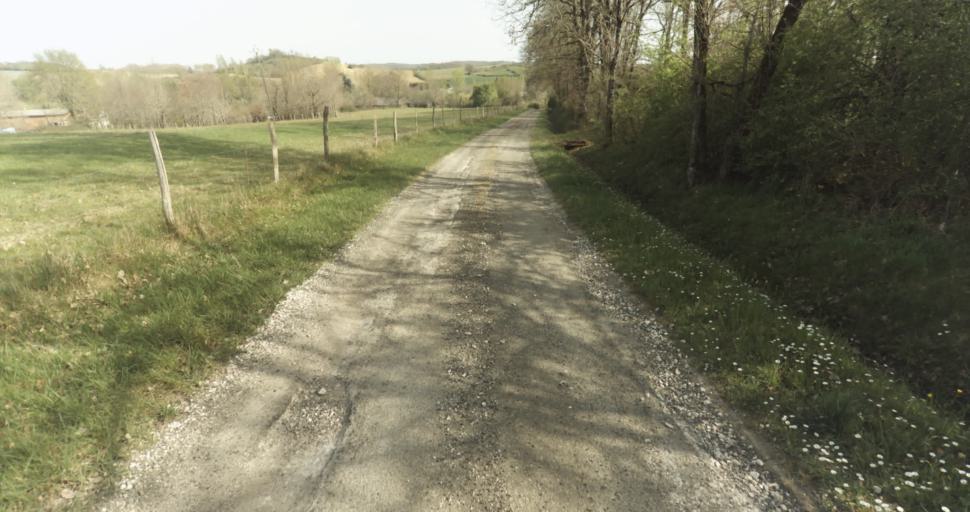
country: FR
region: Midi-Pyrenees
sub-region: Departement du Tarn-et-Garonne
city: Lafrancaise
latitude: 44.1477
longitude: 1.1755
